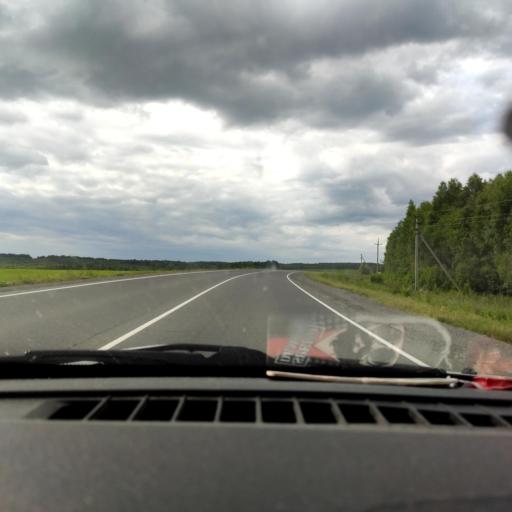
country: RU
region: Perm
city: Verkhnechusovskiye Gorodki
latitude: 58.2177
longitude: 57.1078
